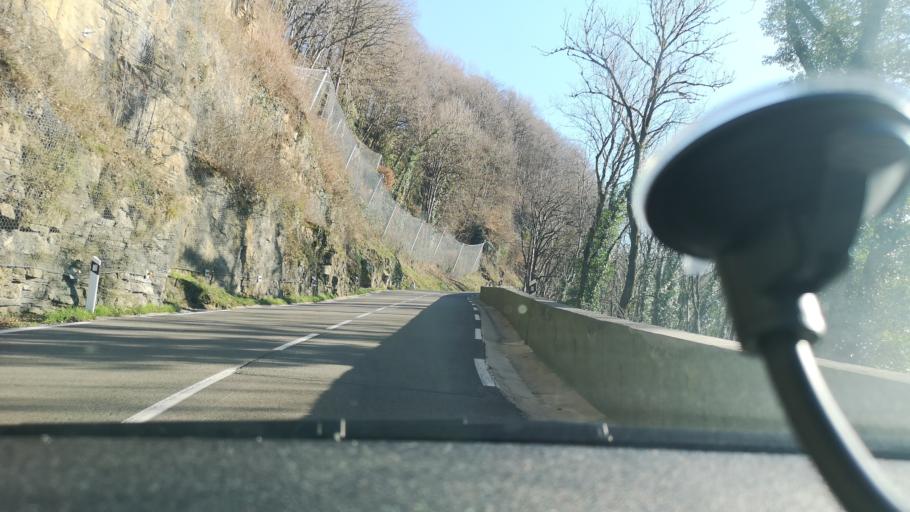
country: FR
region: Franche-Comte
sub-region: Departement du Jura
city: Poligny
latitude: 46.8238
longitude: 5.7330
